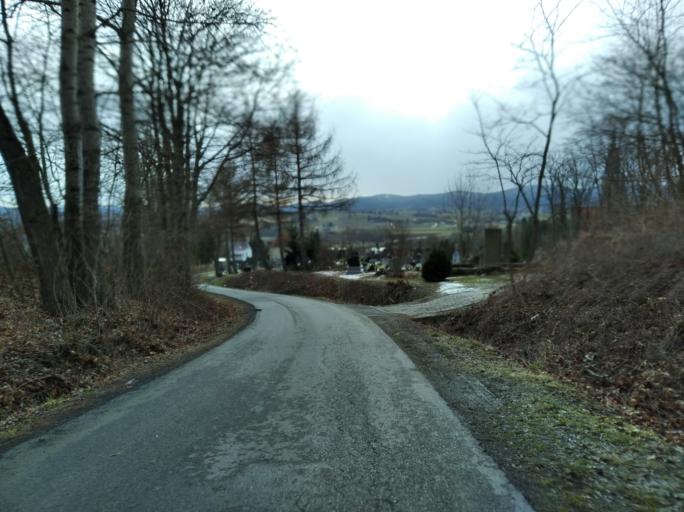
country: PL
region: Subcarpathian Voivodeship
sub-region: Powiat strzyzowski
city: Wysoka Strzyzowska
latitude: 49.8807
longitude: 21.7234
